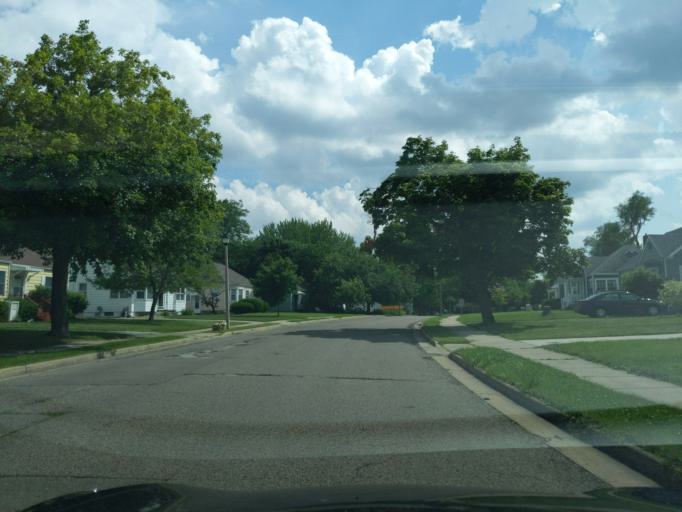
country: US
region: Michigan
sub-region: Ingham County
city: Lansing
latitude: 42.7144
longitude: -84.5750
